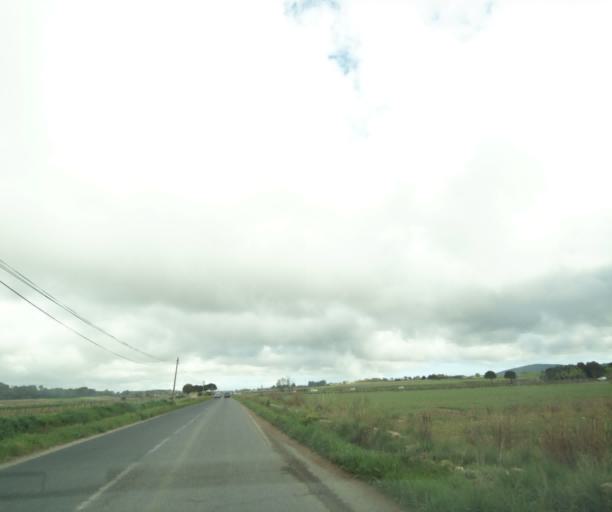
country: FR
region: Languedoc-Roussillon
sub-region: Departement de l'Herault
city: Saussan
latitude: 43.5858
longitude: 3.7744
